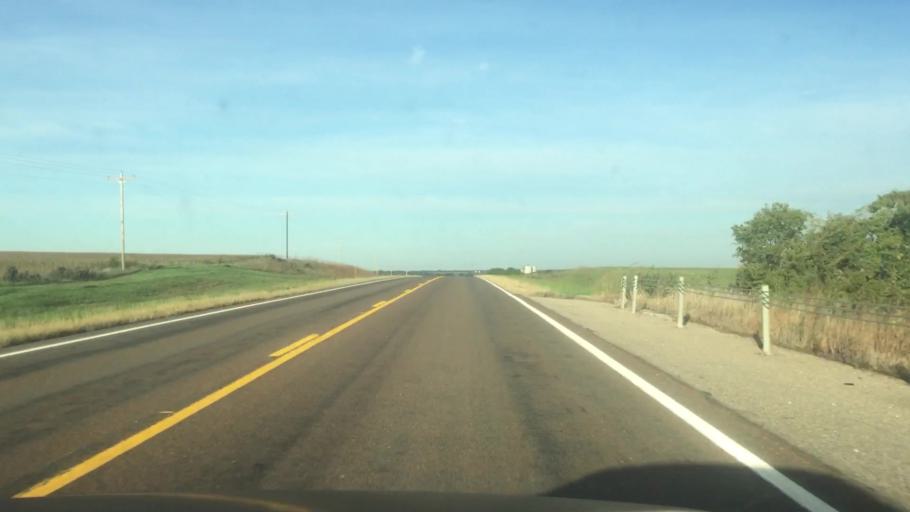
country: US
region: Nebraska
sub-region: Gage County
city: Wymore
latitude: 40.0457
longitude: -96.7658
